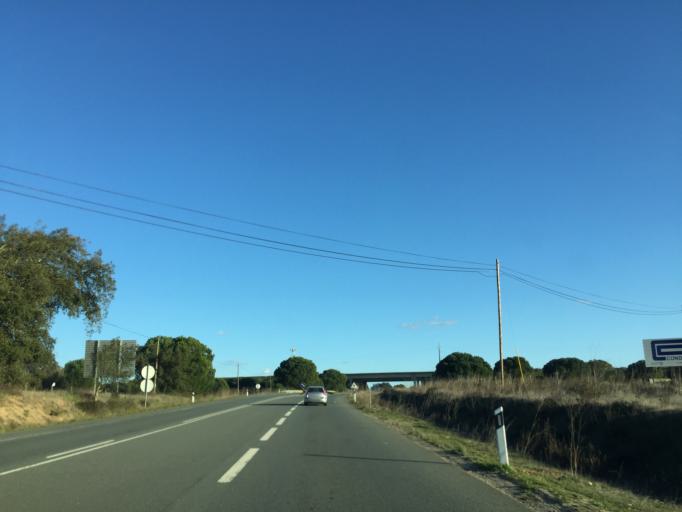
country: PT
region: Setubal
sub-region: Grandola
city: Grandola
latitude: 38.1185
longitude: -8.4225
